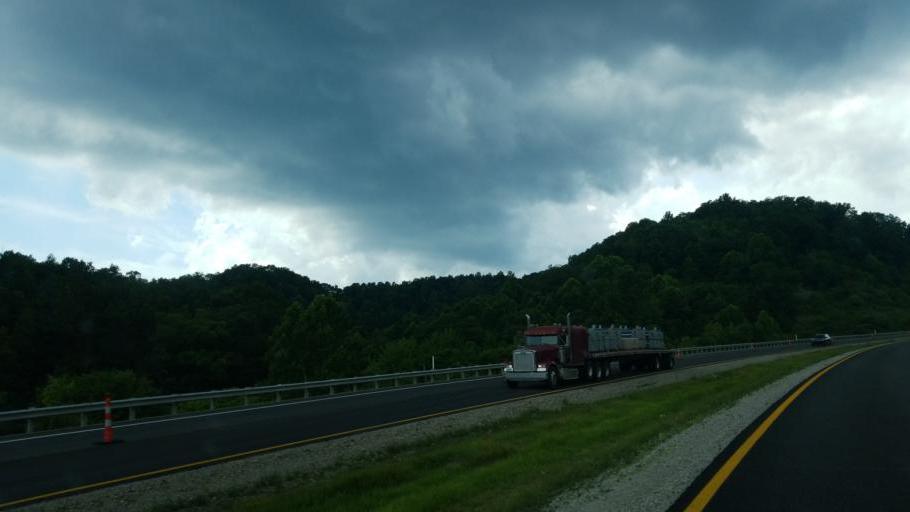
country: US
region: West Virginia
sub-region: Kanawha County
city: Alum Creek
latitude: 38.2652
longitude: -81.8157
